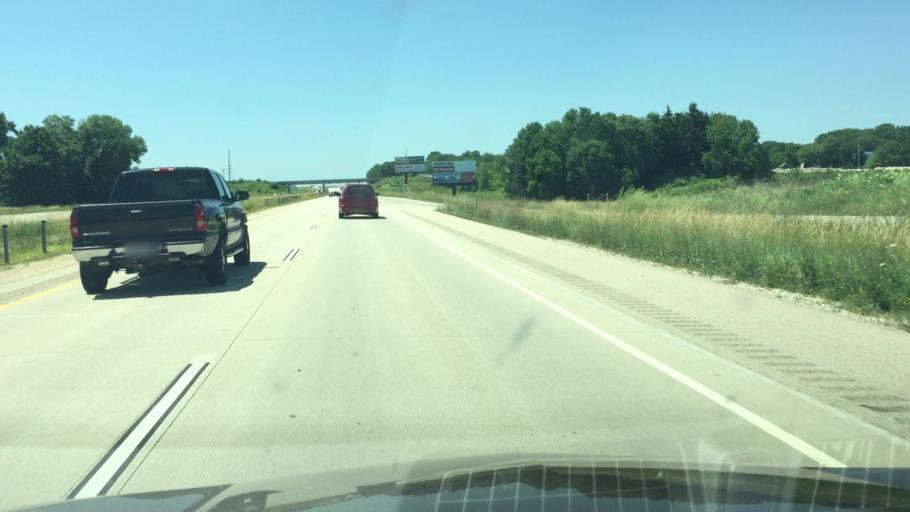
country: US
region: Wisconsin
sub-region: Dodge County
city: Beaver Dam
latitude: 43.4358
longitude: -88.8469
